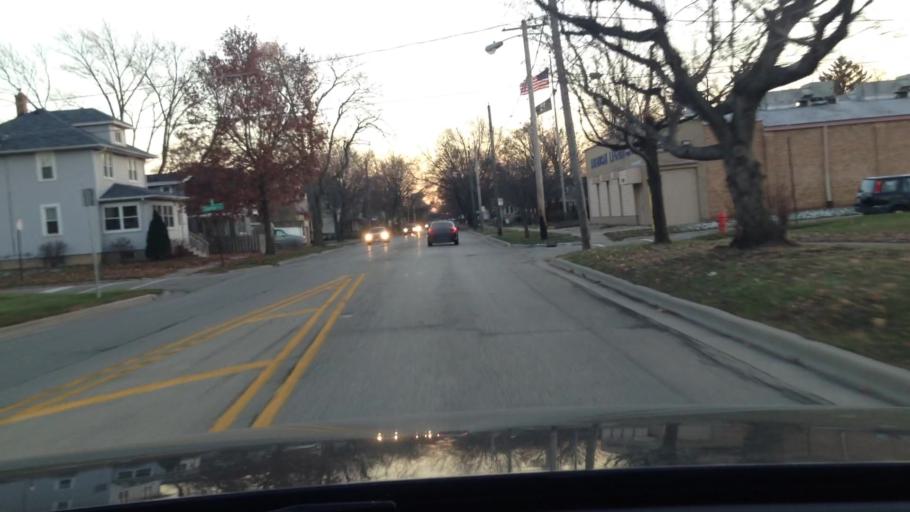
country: US
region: Illinois
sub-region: Kane County
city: Elgin
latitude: 42.0526
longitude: -88.2677
